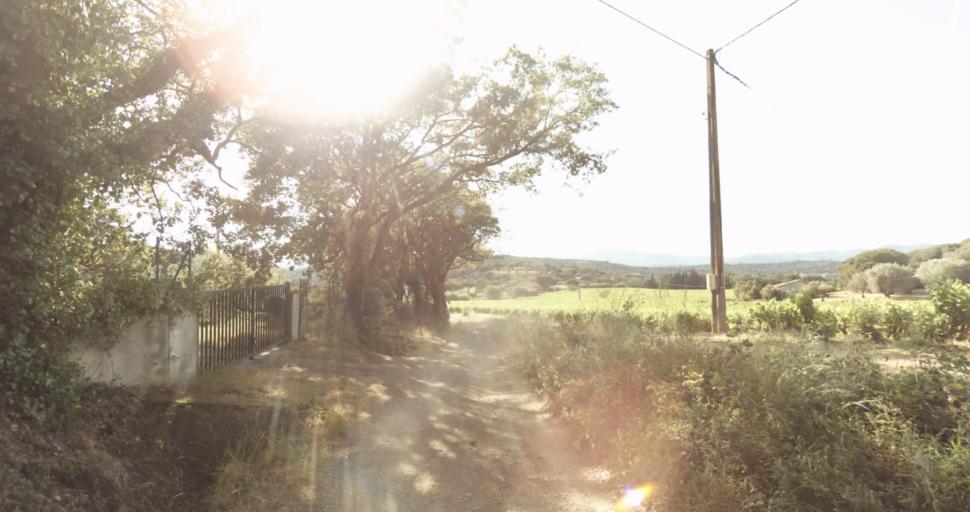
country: FR
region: Provence-Alpes-Cote d'Azur
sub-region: Departement du Var
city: Gassin
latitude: 43.2306
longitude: 6.5801
